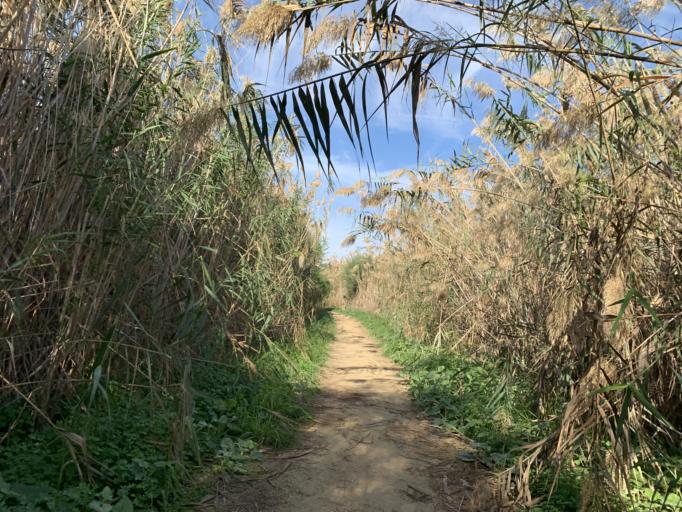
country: CY
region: Larnaka
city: Larnaca
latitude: 34.9099
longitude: 33.6138
